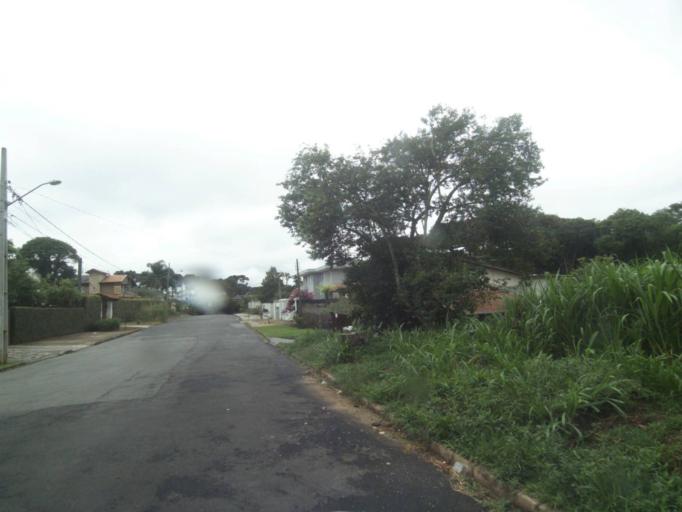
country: BR
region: Parana
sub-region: Curitiba
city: Curitiba
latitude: -25.4226
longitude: -49.3307
